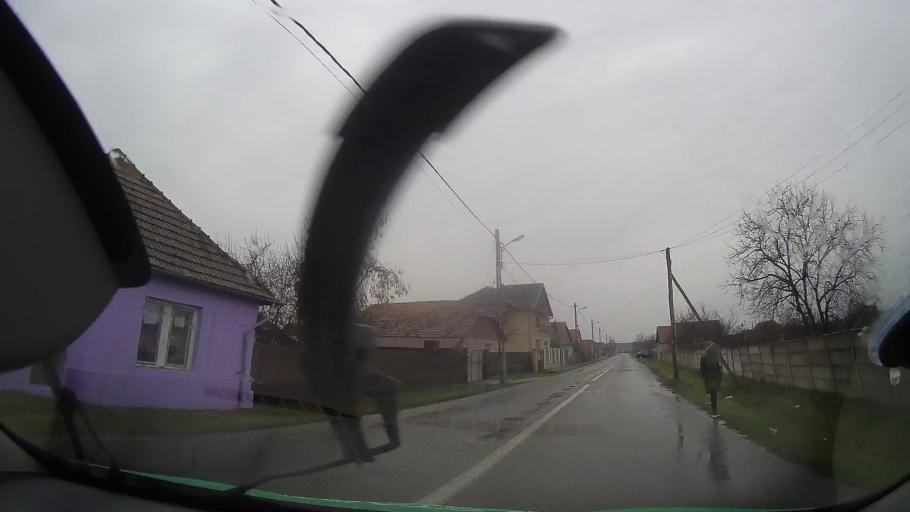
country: RO
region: Bihor
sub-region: Comuna Tinca
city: Gurbediu
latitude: 46.7902
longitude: 21.8551
